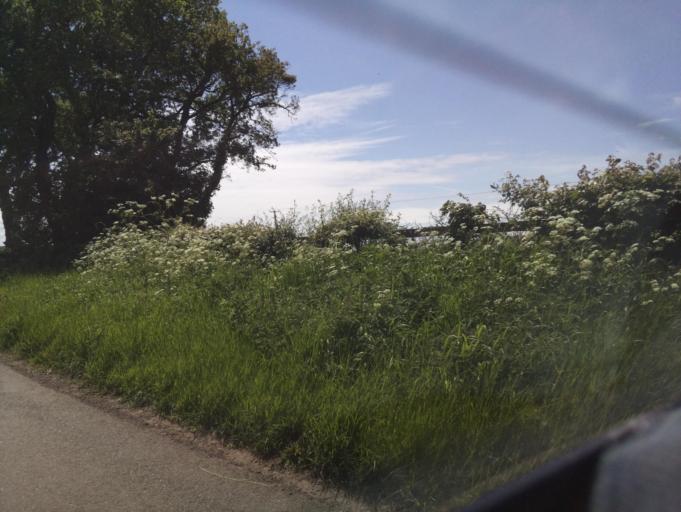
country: GB
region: Wales
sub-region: Monmouthshire
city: Caldicot
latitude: 51.6337
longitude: -2.7460
